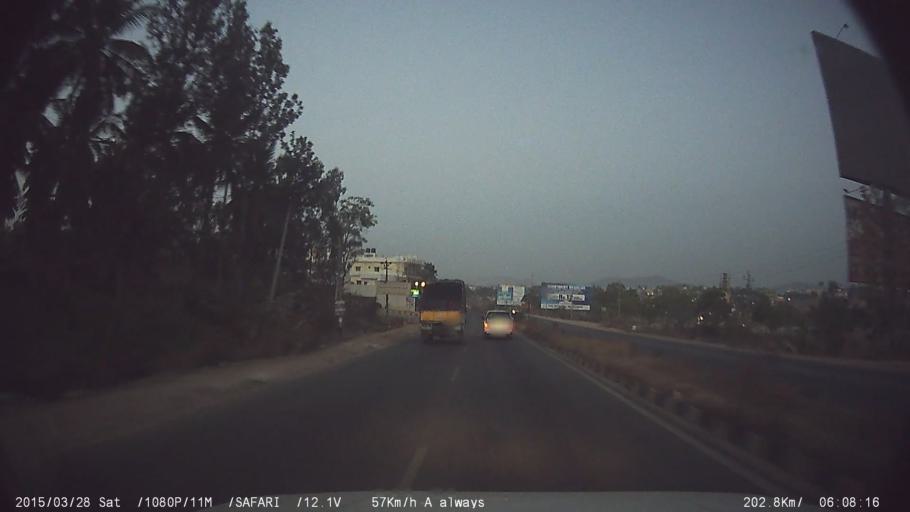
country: IN
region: Karnataka
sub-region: Ramanagara
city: Ramanagaram
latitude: 12.8018
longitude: 77.3959
